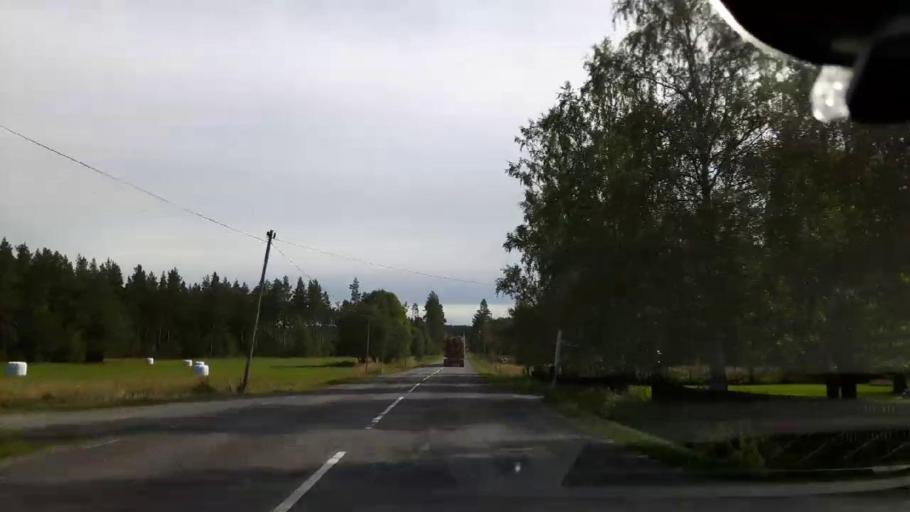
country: SE
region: Jaemtland
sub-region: Ragunda Kommun
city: Hammarstrand
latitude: 63.1480
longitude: 15.8433
